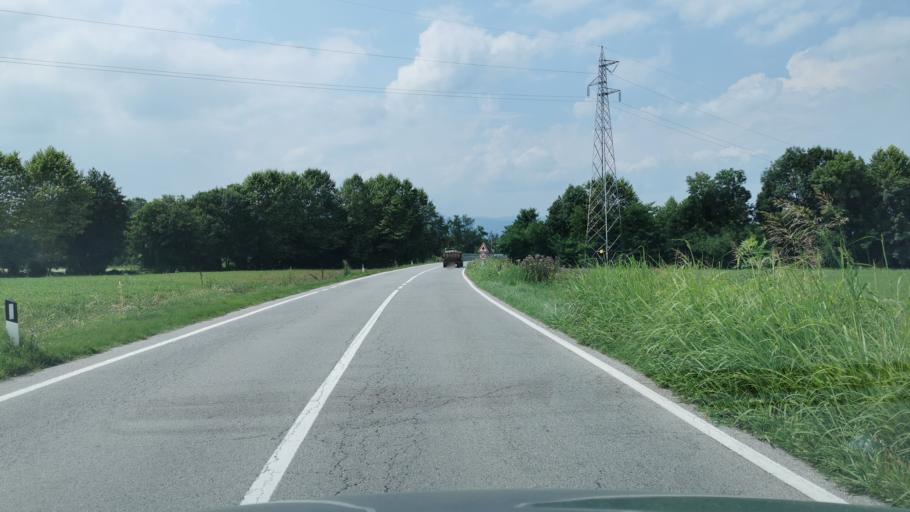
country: IT
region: Piedmont
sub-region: Provincia di Cuneo
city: Roata Rossi
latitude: 44.4349
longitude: 7.5003
